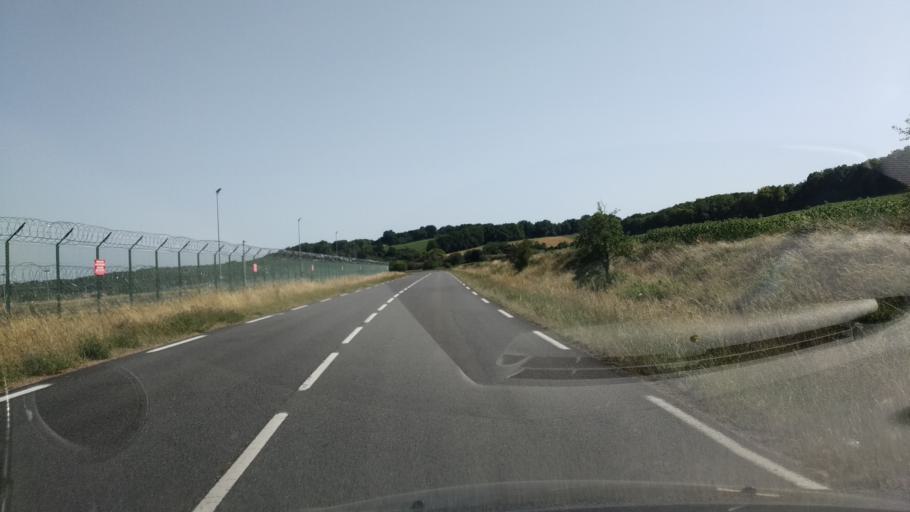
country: FR
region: Poitou-Charentes
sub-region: Departement de la Vienne
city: Lussac-les-Chateaux
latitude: 46.4546
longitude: 0.6478
